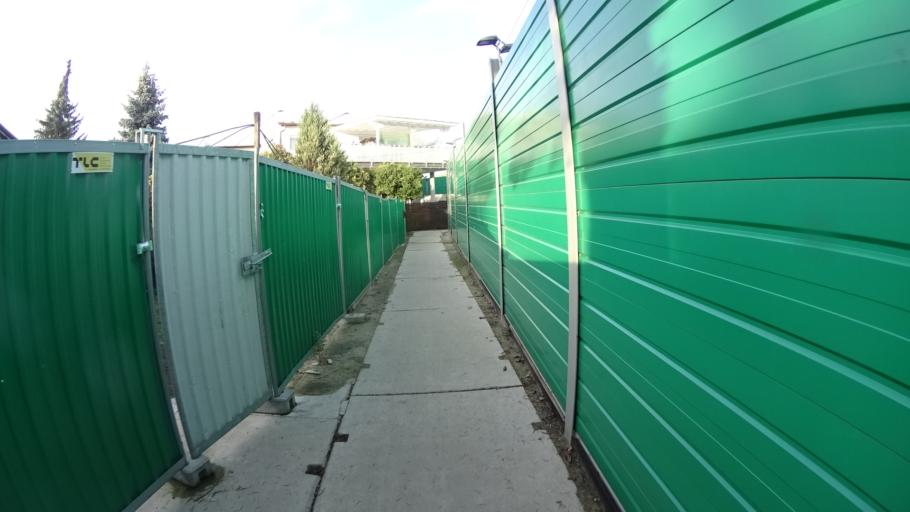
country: PL
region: Masovian Voivodeship
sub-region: Warszawa
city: Targowek
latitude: 52.2846
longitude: 21.0616
